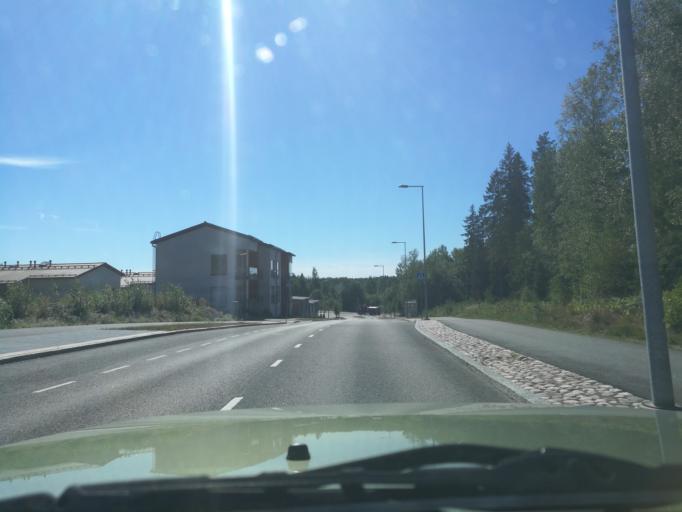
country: FI
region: Uusimaa
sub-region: Helsinki
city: Kerava
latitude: 60.3508
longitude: 25.1327
